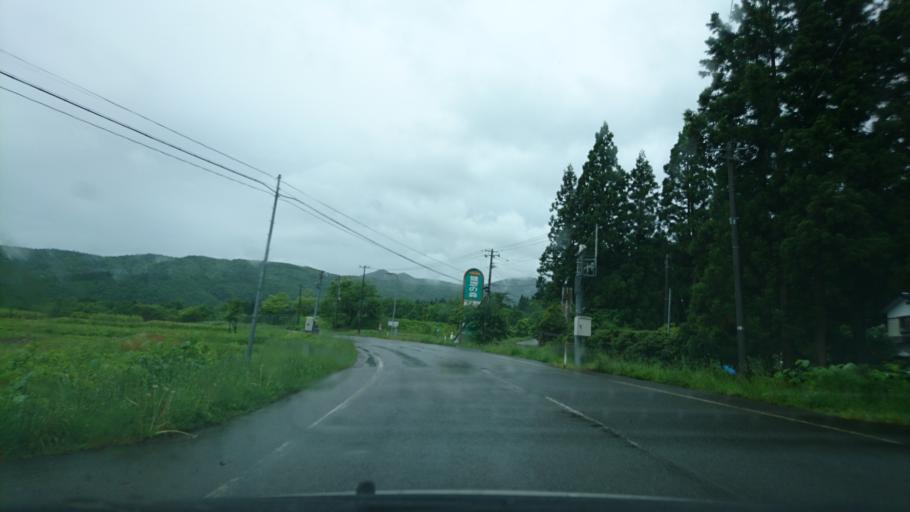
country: JP
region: Iwate
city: Ichinoseki
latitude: 39.0124
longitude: 140.8663
